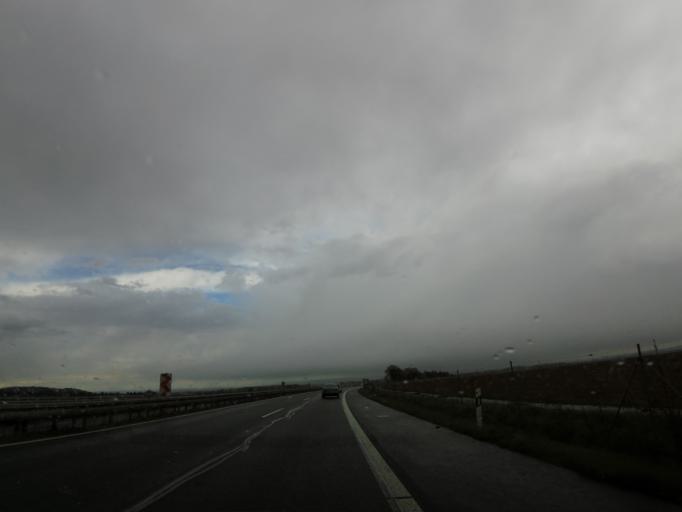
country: DE
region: Lower Saxony
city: Vienenburg
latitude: 51.9317
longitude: 10.5658
